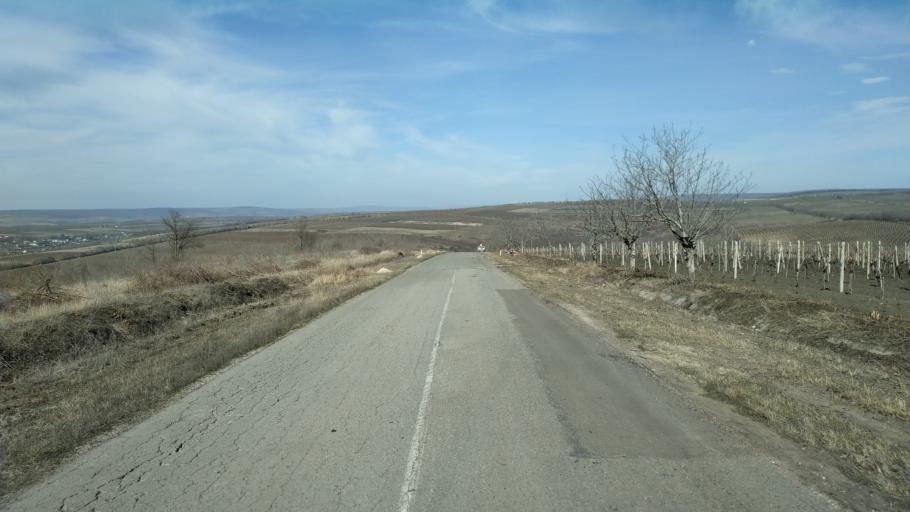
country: MD
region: Nisporeni
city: Nisporeni
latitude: 46.9529
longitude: 28.2376
